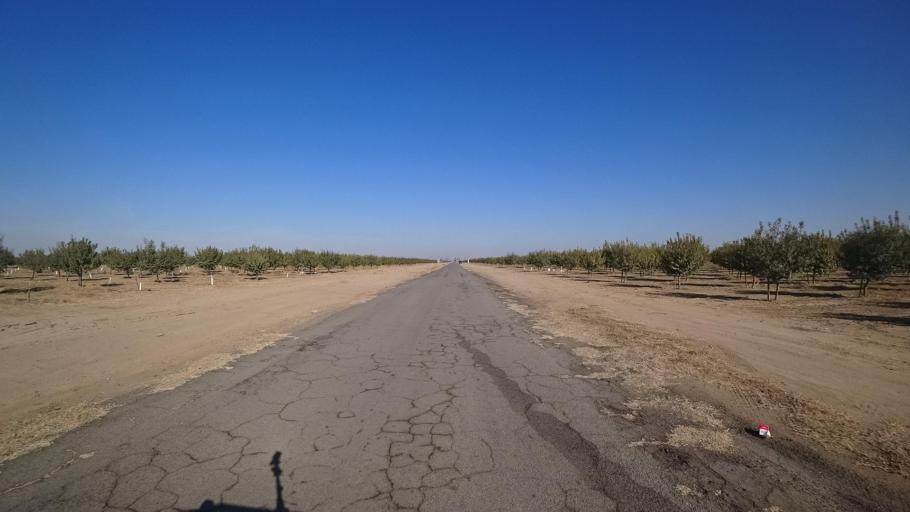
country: US
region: California
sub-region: Kern County
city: Delano
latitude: 35.7482
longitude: -119.2319
